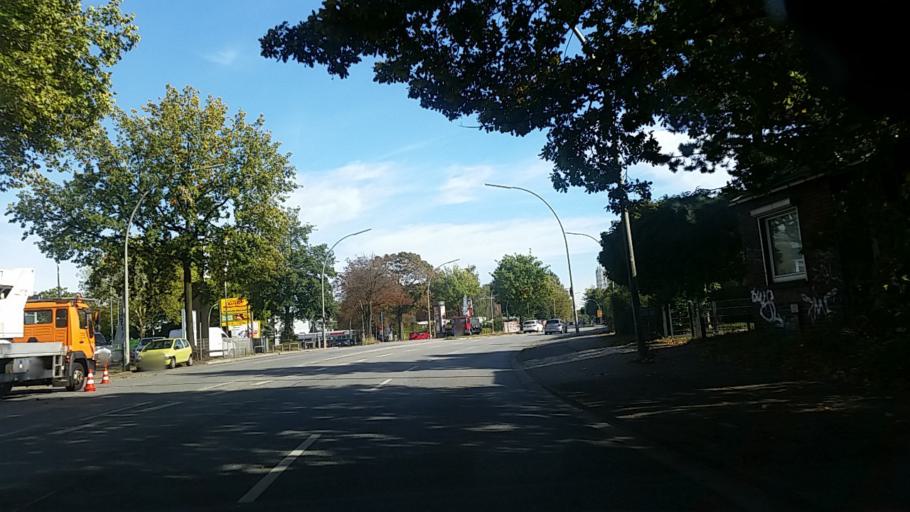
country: DE
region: Hamburg
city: Stellingen
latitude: 53.5916
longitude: 9.9225
